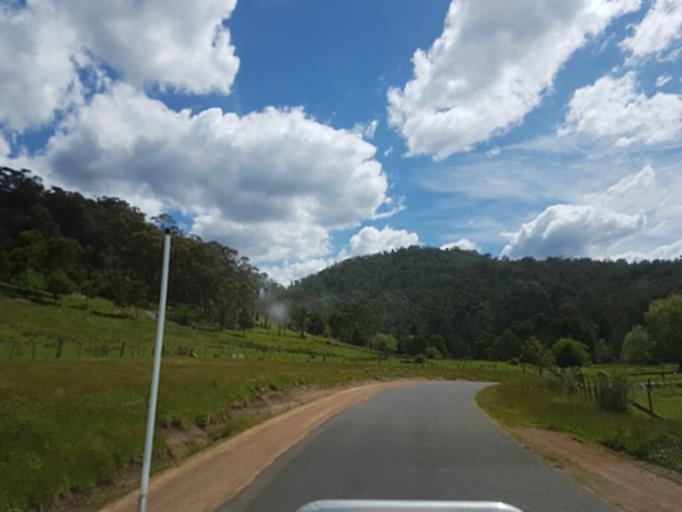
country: AU
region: Victoria
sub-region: East Gippsland
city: Bairnsdale
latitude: -37.4263
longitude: 147.2499
